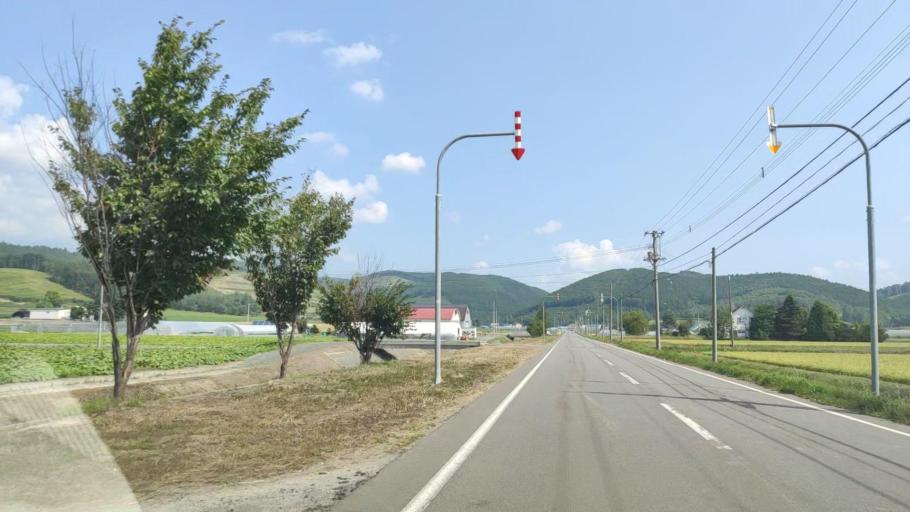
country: JP
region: Hokkaido
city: Shimo-furano
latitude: 43.4108
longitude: 142.3978
